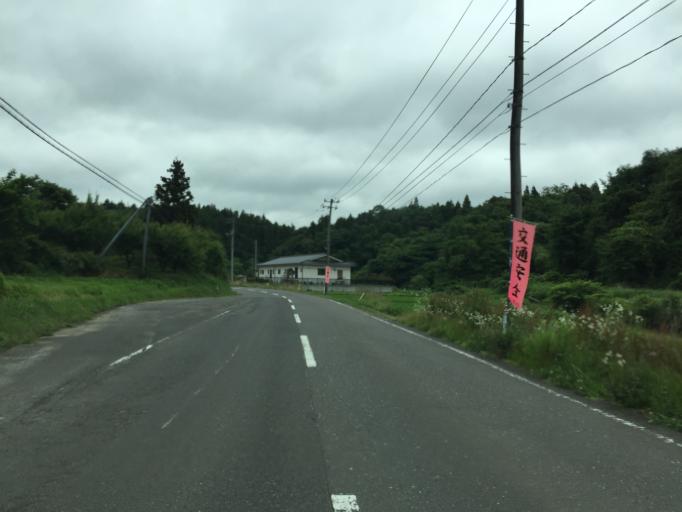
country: JP
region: Fukushima
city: Ishikawa
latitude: 37.1798
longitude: 140.5506
